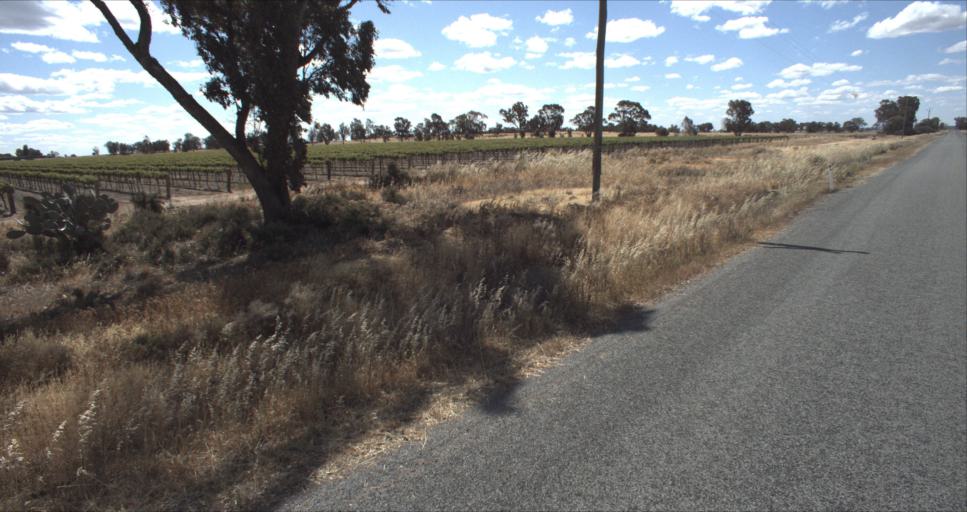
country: AU
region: New South Wales
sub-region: Leeton
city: Leeton
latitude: -34.4937
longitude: 146.2468
